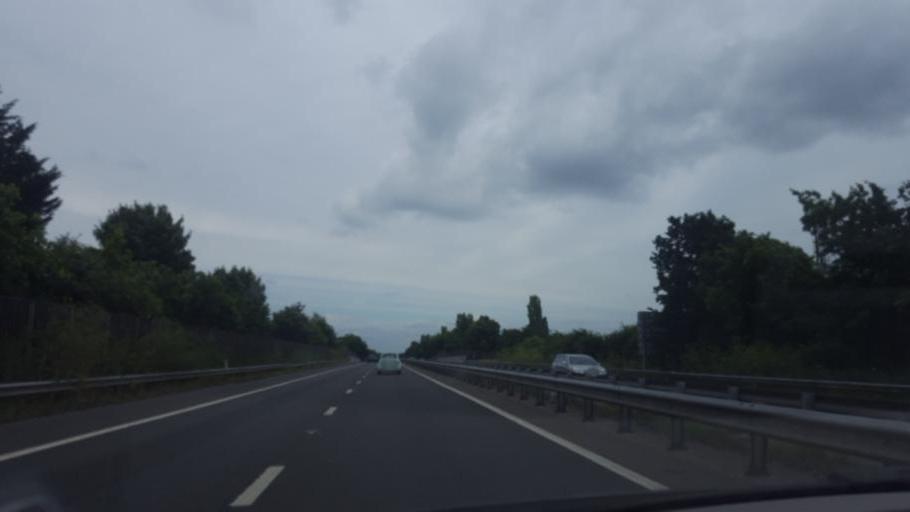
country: GB
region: England
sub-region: Royal Borough of Windsor and Maidenhead
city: White Waltham
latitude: 51.5122
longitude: -0.7544
